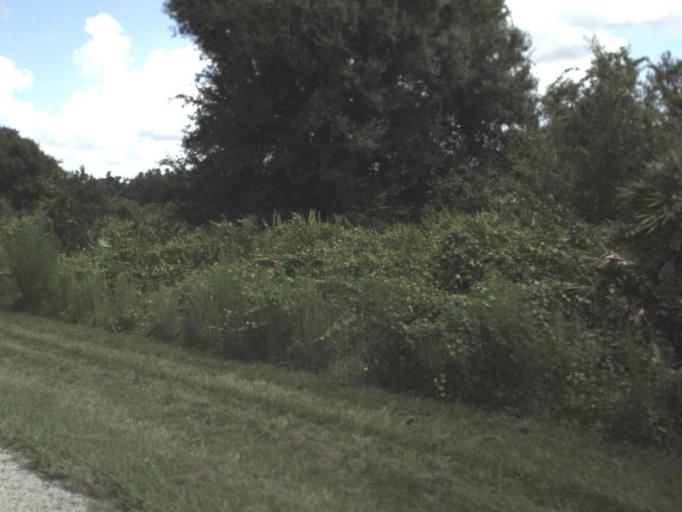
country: US
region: Florida
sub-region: Hardee County
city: Zolfo Springs
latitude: 27.4007
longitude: -81.7950
